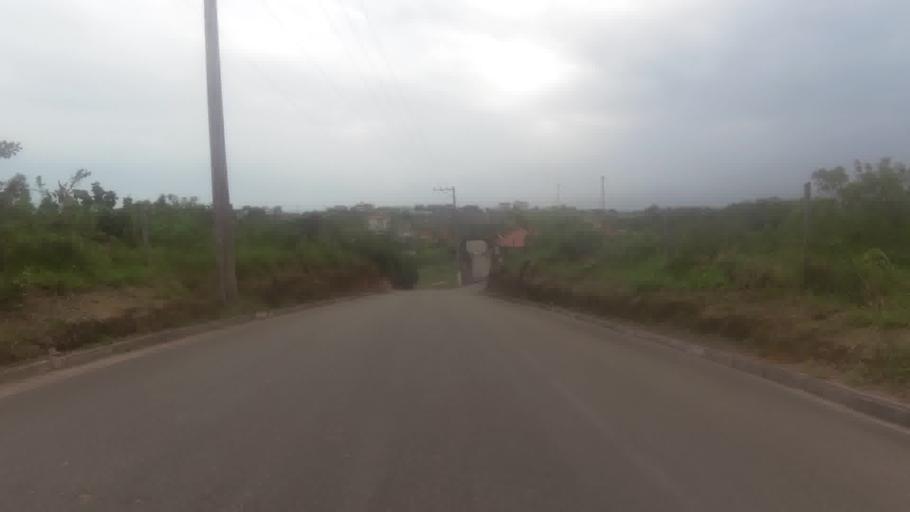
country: BR
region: Espirito Santo
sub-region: Piuma
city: Piuma
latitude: -20.7995
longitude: -40.5939
